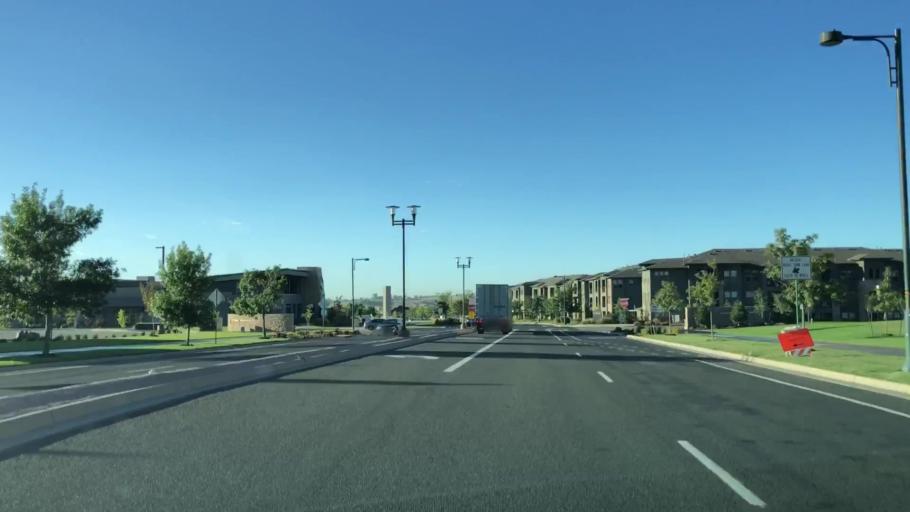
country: US
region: Colorado
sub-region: Larimer County
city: Loveland
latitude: 40.4045
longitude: -104.9834
